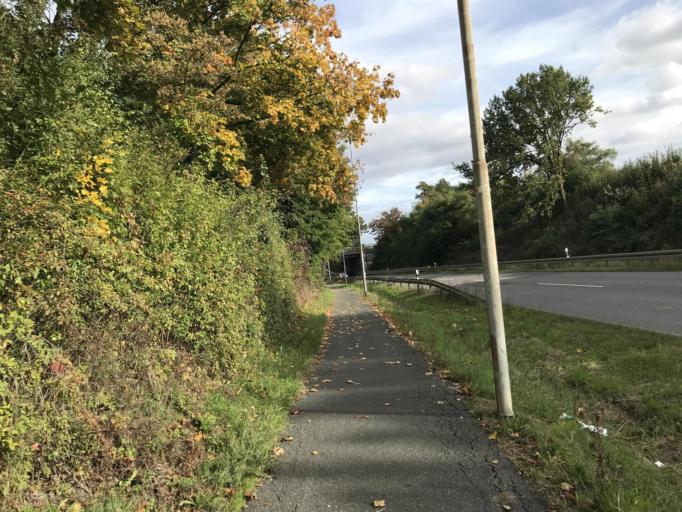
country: DE
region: Hesse
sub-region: Regierungsbezirk Darmstadt
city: Butzbach
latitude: 50.4250
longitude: 8.6689
